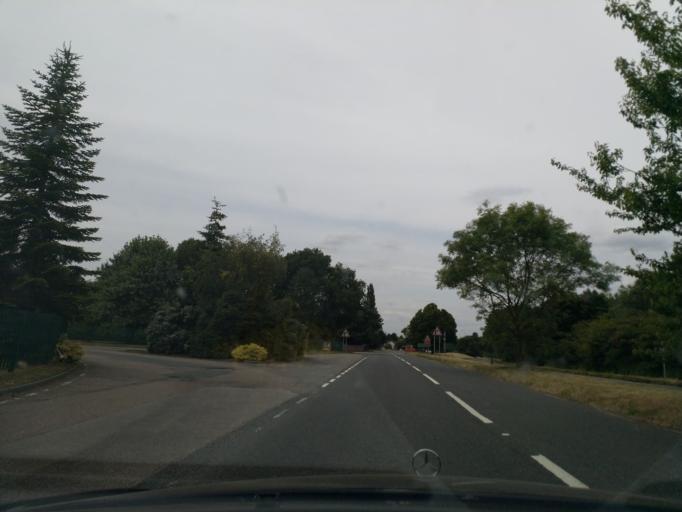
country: GB
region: England
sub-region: Solihull
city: Balsall Common
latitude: 52.4108
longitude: -1.6687
